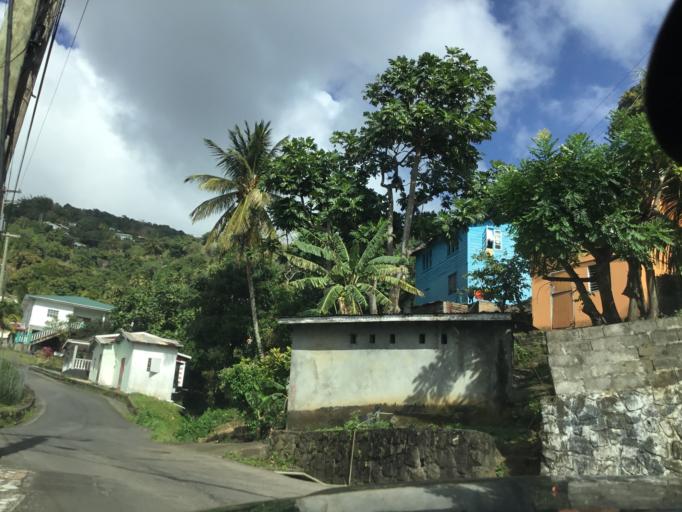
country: VC
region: Saint George
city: Kingstown
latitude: 13.1614
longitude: -61.2181
